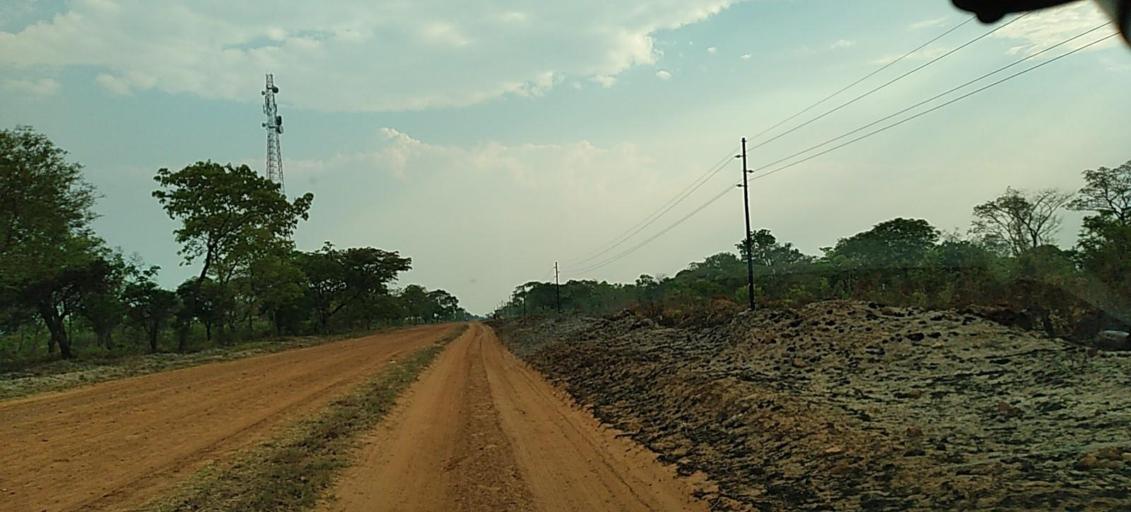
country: ZM
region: North-Western
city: Kabompo
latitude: -13.8841
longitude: 23.6625
